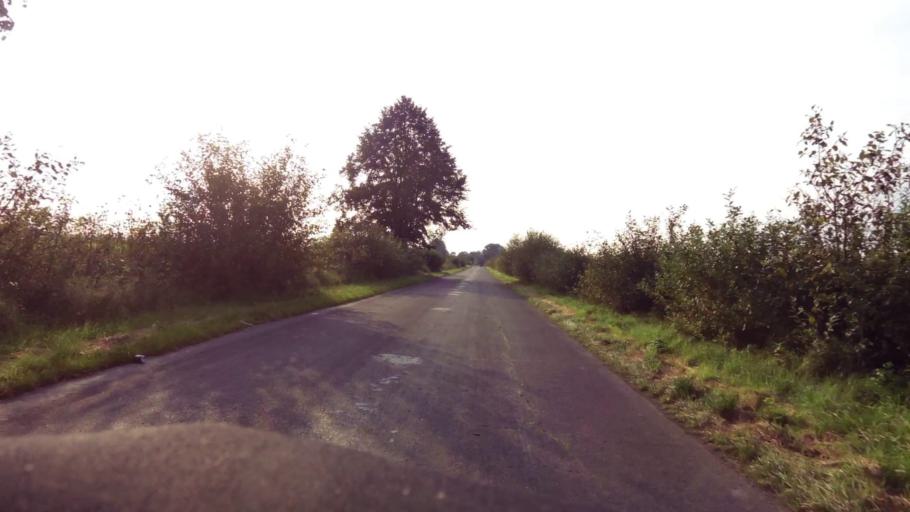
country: PL
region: West Pomeranian Voivodeship
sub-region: Powiat stargardzki
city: Dobrzany
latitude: 53.3396
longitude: 15.3712
